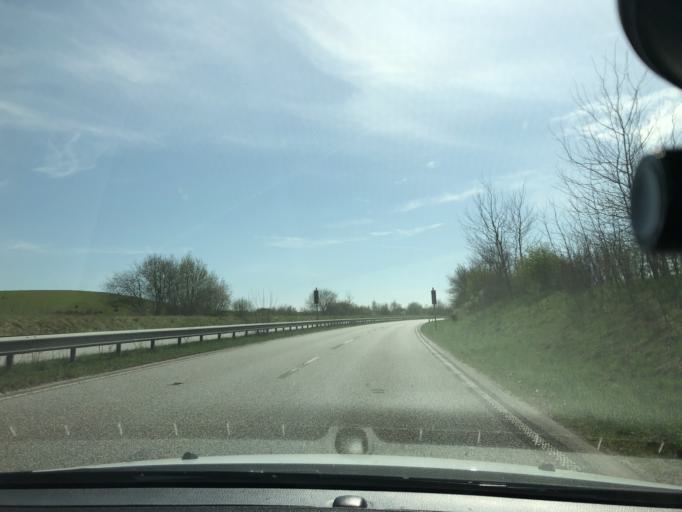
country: DE
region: Schleswig-Holstein
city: Tastrup
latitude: 54.7677
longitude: 9.4605
